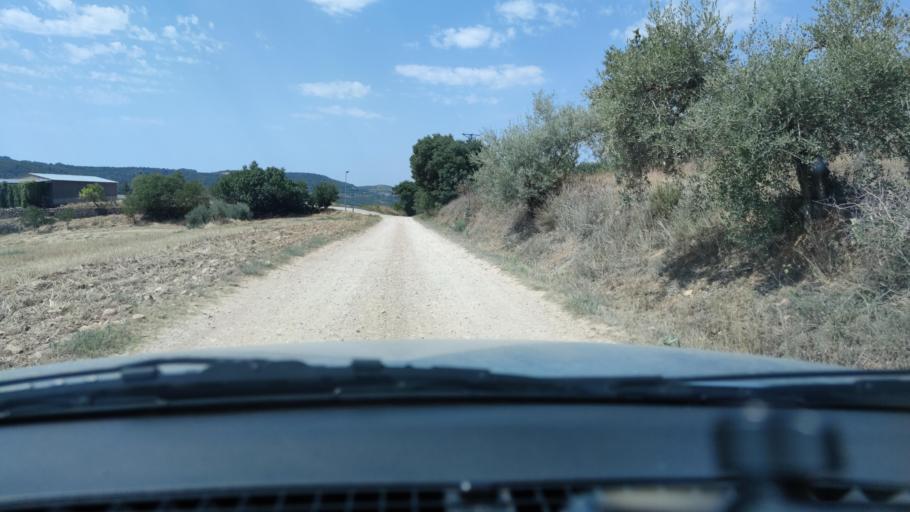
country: ES
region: Catalonia
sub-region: Provincia de Lleida
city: Ager
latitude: 41.9311
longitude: 0.8014
